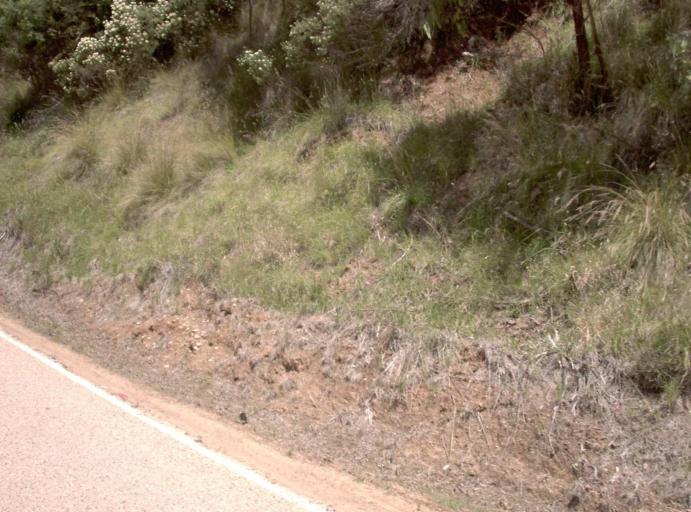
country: AU
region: Victoria
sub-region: East Gippsland
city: Bairnsdale
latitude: -37.5272
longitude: 147.8433
